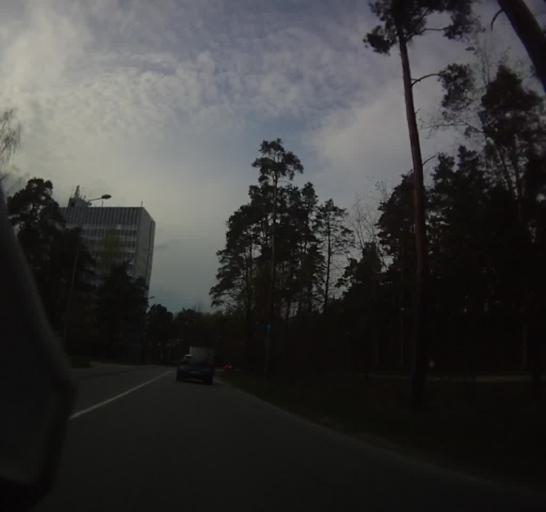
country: LV
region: Riga
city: Jaunciems
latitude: 56.9817
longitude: 24.2108
